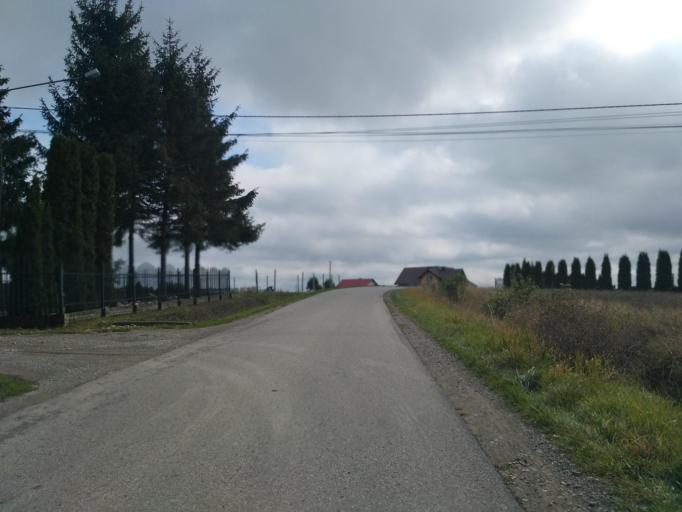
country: PL
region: Subcarpathian Voivodeship
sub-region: Powiat ropczycko-sedziszowski
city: Niedzwiada
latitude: 49.9623
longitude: 21.4500
